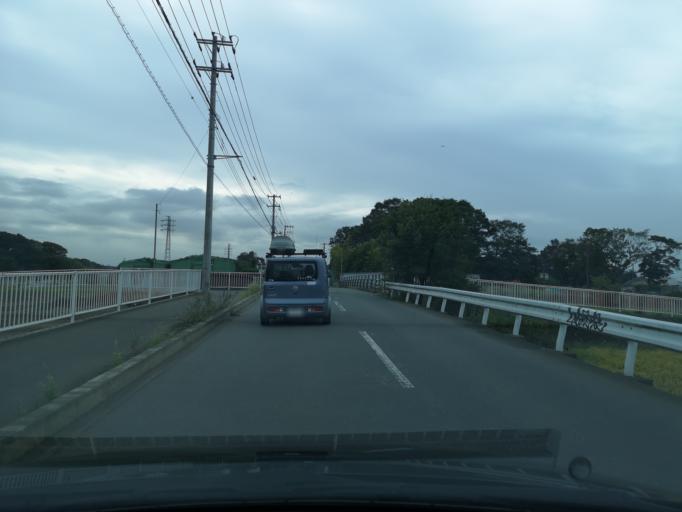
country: JP
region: Kanagawa
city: Atsugi
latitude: 35.3888
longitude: 139.3917
